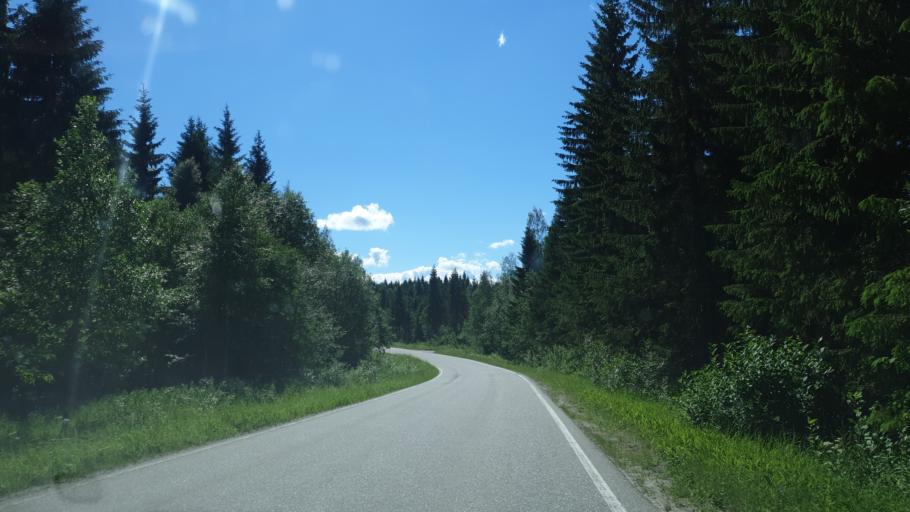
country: FI
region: Northern Savo
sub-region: Koillis-Savo
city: Kaavi
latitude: 63.0066
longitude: 28.5046
